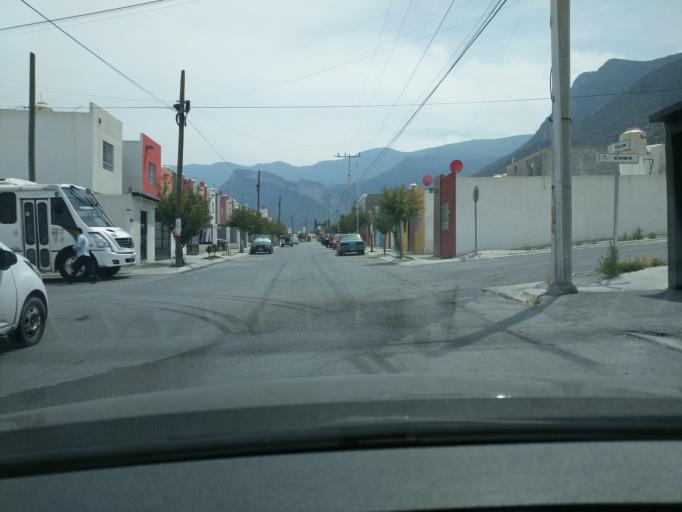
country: MX
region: Coahuila
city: Saltillo
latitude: 25.3458
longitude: -101.0078
